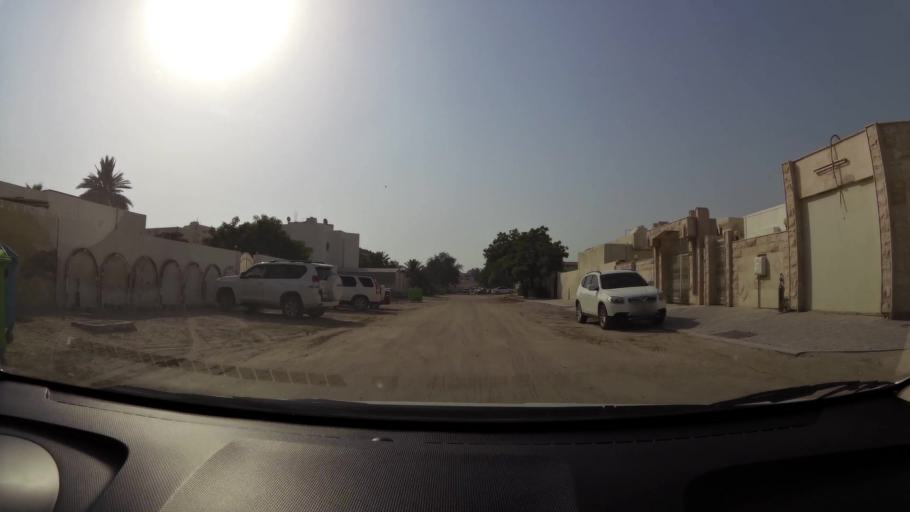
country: AE
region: Ajman
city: Ajman
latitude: 25.3798
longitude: 55.4209
